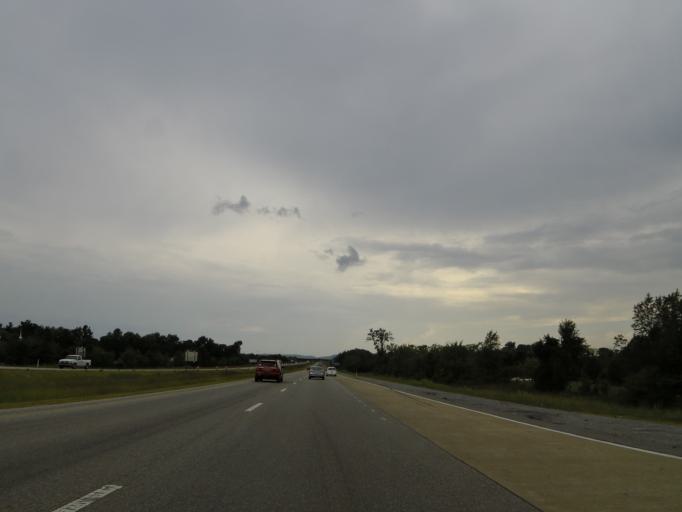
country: US
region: Tennessee
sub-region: Rutherford County
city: Murfreesboro
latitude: 35.8804
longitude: -86.4825
